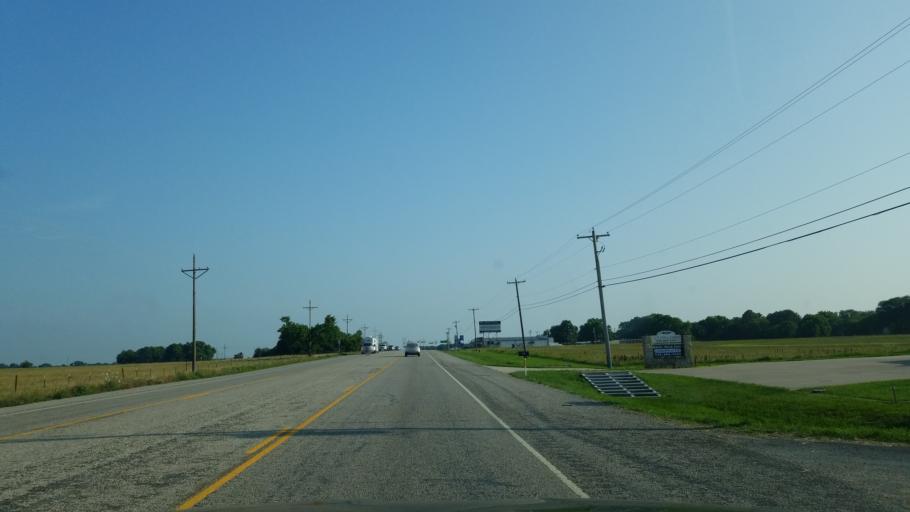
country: US
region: Texas
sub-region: Denton County
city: Pilot Point
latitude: 33.3994
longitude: -96.9449
